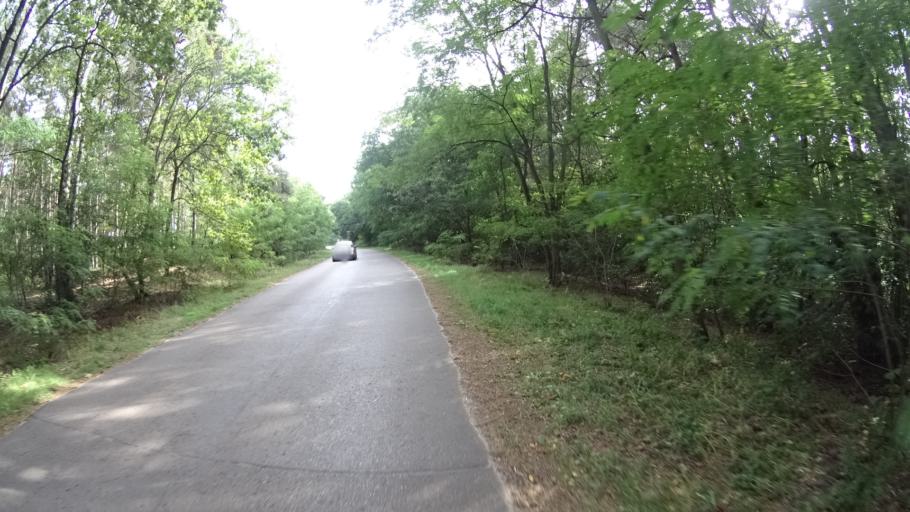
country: PL
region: Masovian Voivodeship
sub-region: Powiat legionowski
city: Serock
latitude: 52.4914
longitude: 21.0867
